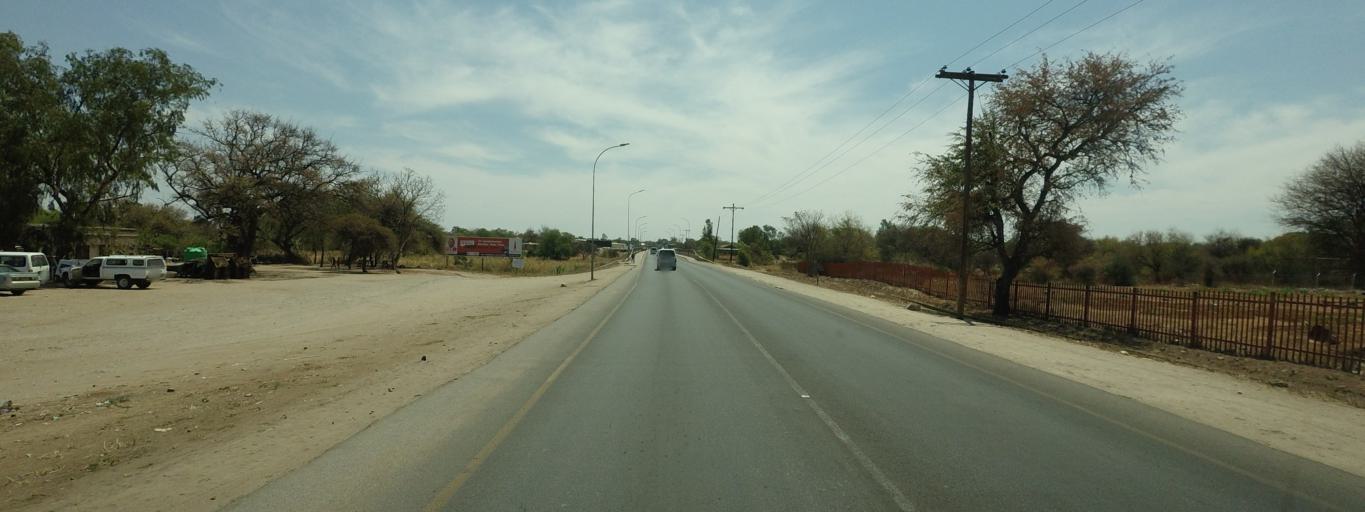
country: BW
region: North East
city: Francistown
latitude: -21.1711
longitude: 27.5015
